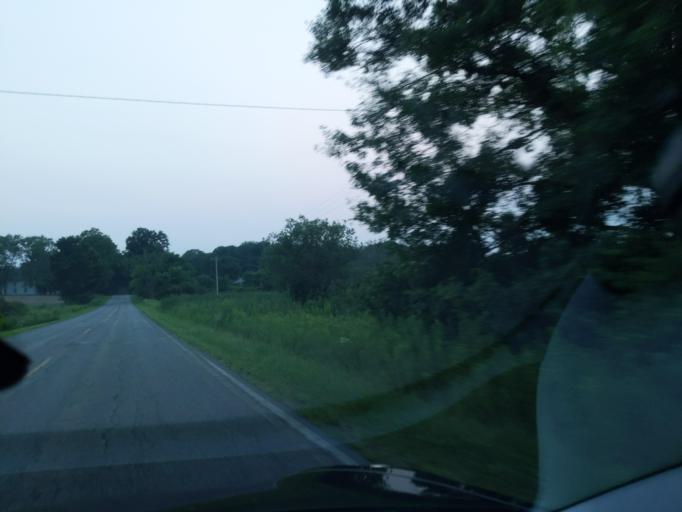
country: US
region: Michigan
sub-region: Ingham County
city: Leslie
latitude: 42.3716
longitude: -84.5076
